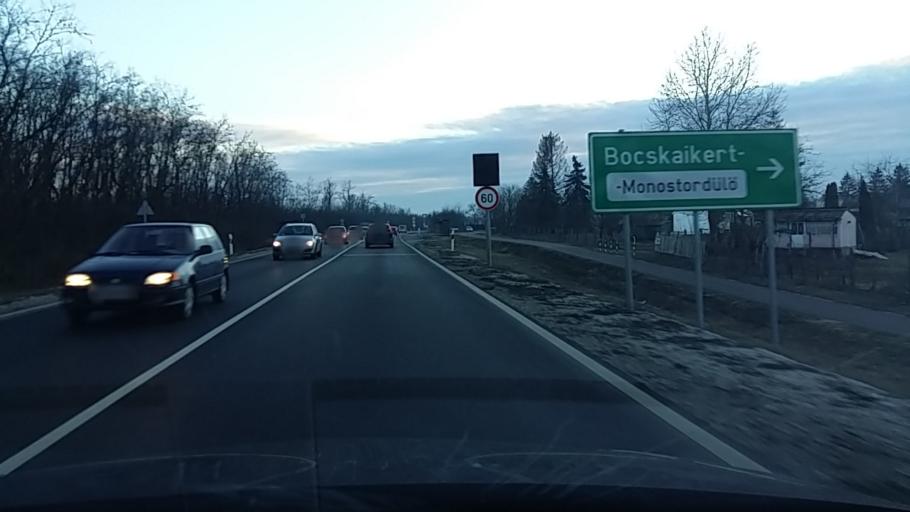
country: HU
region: Hajdu-Bihar
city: Hajduhadhaz
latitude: 47.6248
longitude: 21.6600
